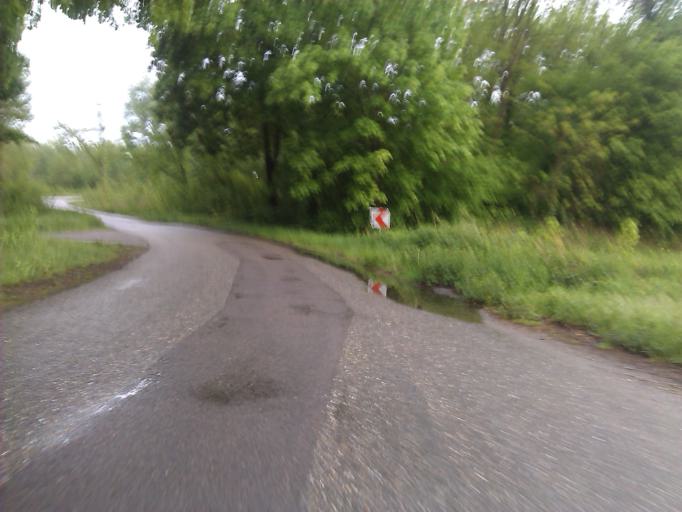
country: FR
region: Alsace
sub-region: Departement du Bas-Rhin
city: Drusenheim
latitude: 48.7553
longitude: 7.9726
